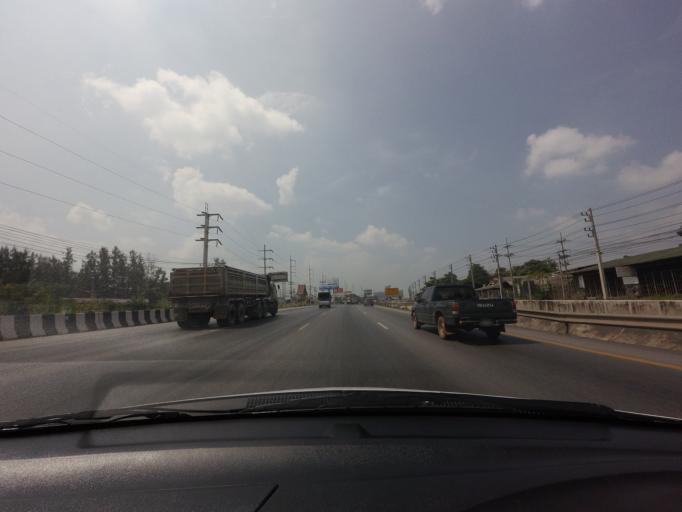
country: TH
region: Nakhon Ratchasima
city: Pak Chong
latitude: 14.6531
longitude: 101.3627
